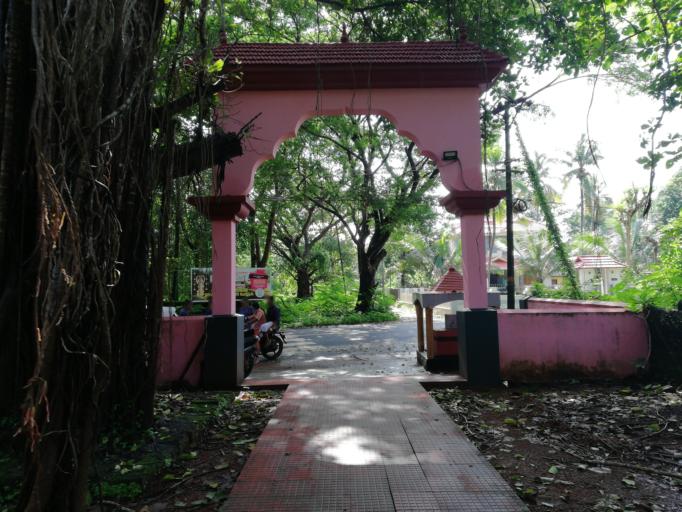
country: IN
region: Kerala
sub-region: Kannur
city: Payyannur
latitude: 12.0563
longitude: 75.1899
